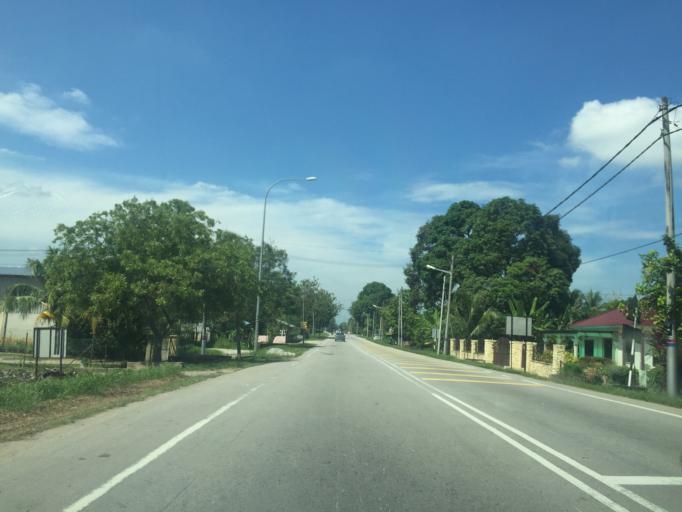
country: MY
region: Penang
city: Tasek Glugor
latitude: 5.4876
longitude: 100.4766
